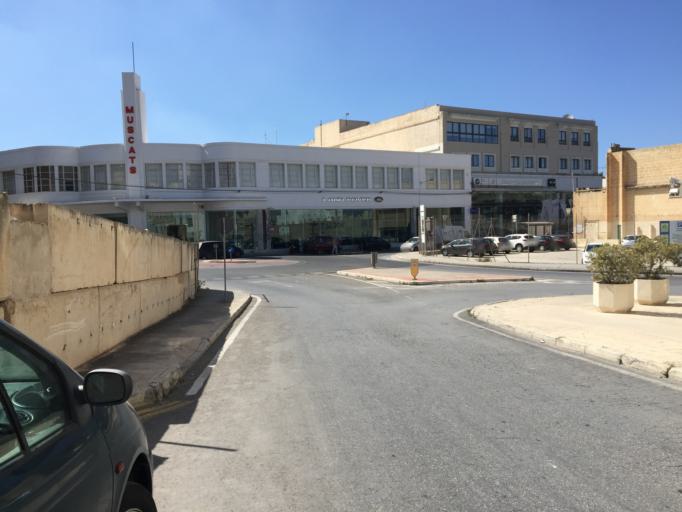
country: MT
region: Ta' Xbiex
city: Ta' Xbiex
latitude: 35.9011
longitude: 14.4919
